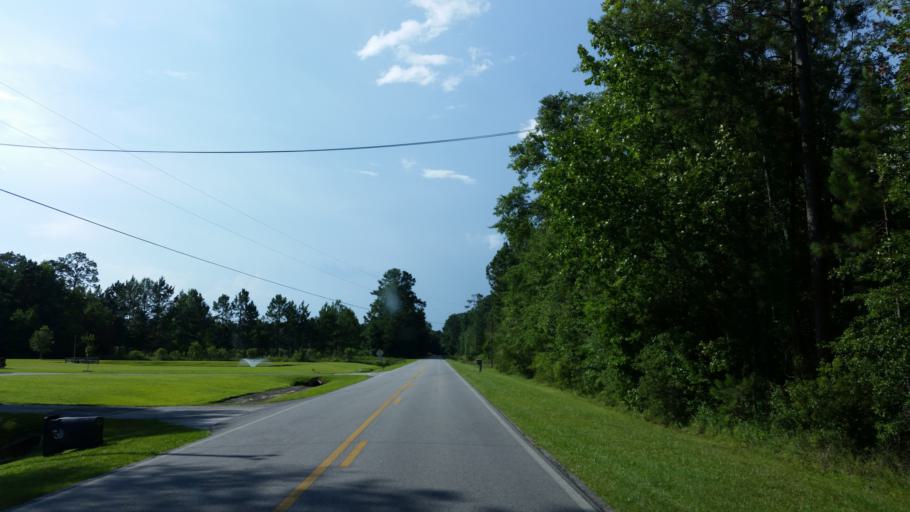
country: US
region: Georgia
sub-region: Lowndes County
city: Hahira
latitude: 30.9423
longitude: -83.4082
